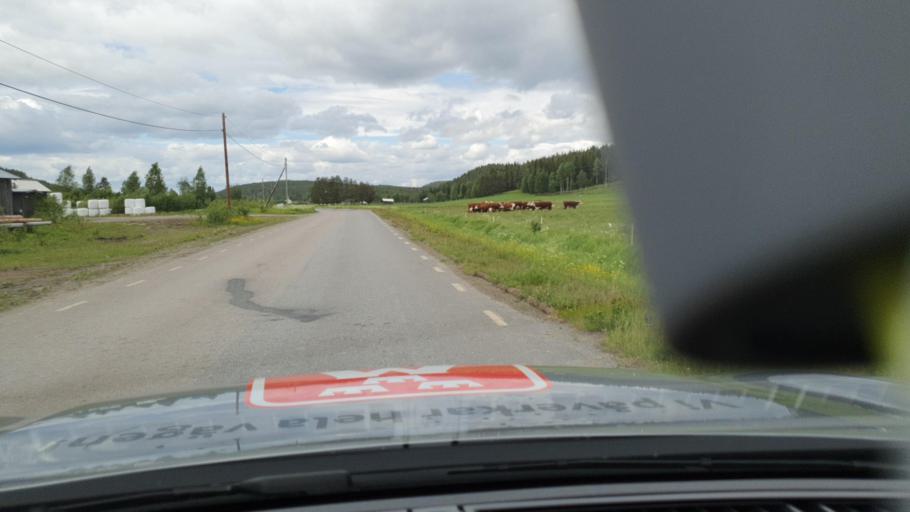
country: SE
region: Norrbotten
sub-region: Lulea Kommun
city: Sodra Sunderbyn
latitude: 65.8609
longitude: 21.9134
